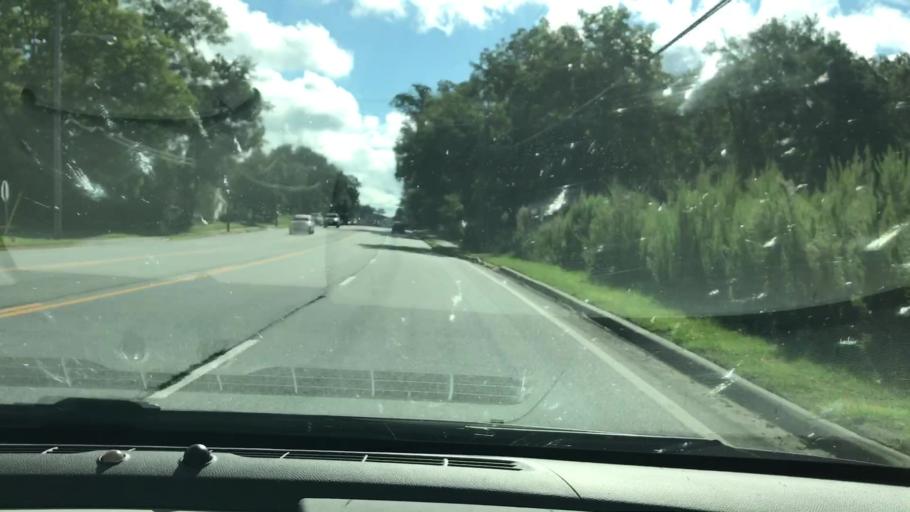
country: US
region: Georgia
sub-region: Worth County
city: Sylvester
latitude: 31.5309
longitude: -83.8502
